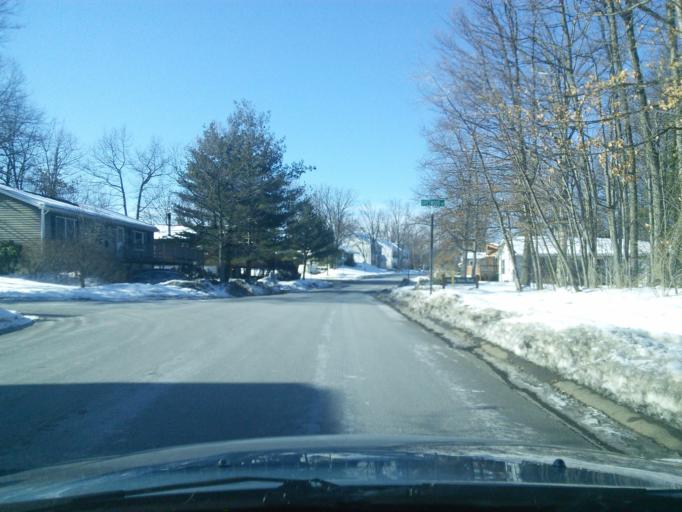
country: US
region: Pennsylvania
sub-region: Centre County
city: Park Forest Village
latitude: 40.8105
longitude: -77.9285
